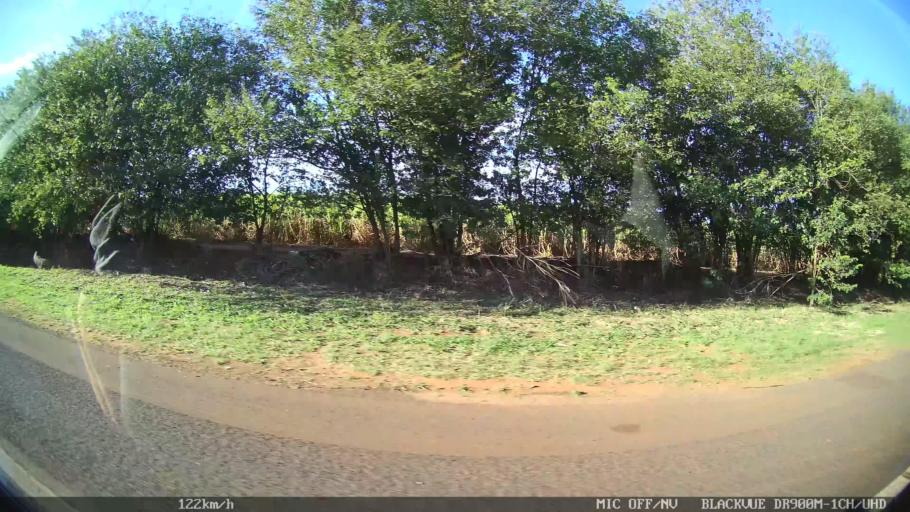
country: BR
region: Sao Paulo
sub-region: Americo Brasiliense
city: Americo Brasiliense
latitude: -21.7649
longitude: -48.1116
